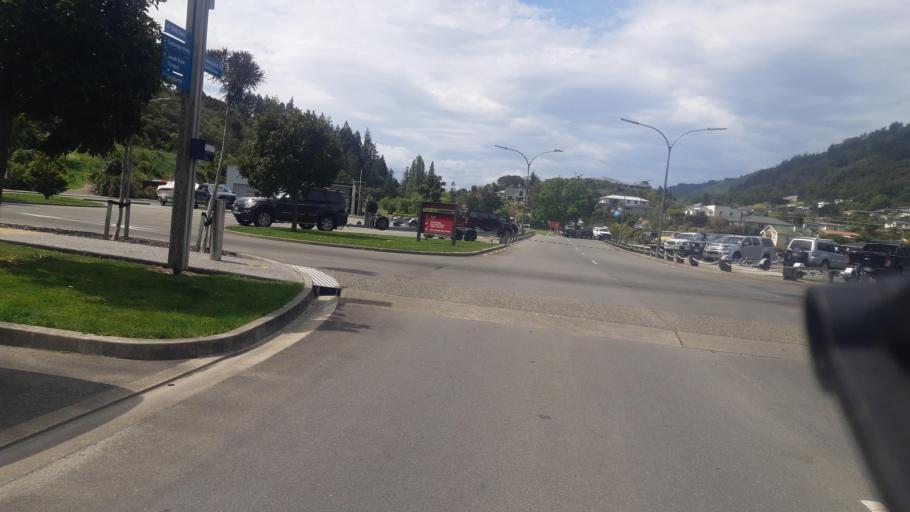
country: NZ
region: Marlborough
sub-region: Marlborough District
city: Picton
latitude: -41.2877
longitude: 174.0129
